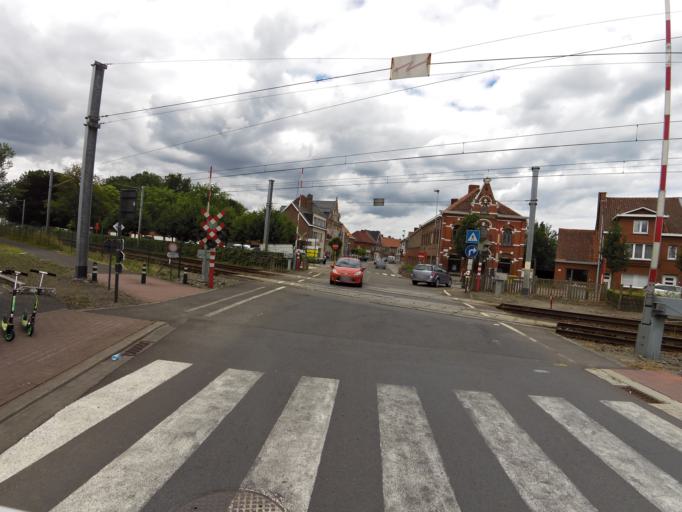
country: BE
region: Flanders
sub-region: Provincie West-Vlaanderen
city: Kortemark
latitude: 51.0249
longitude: 3.0426
